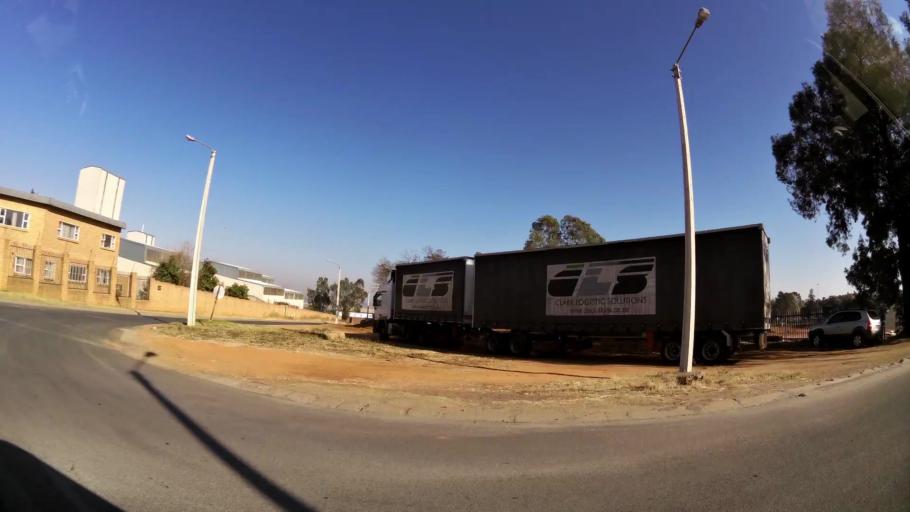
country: ZA
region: Gauteng
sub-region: City of Johannesburg Metropolitan Municipality
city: Modderfontein
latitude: -26.0613
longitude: 28.1772
